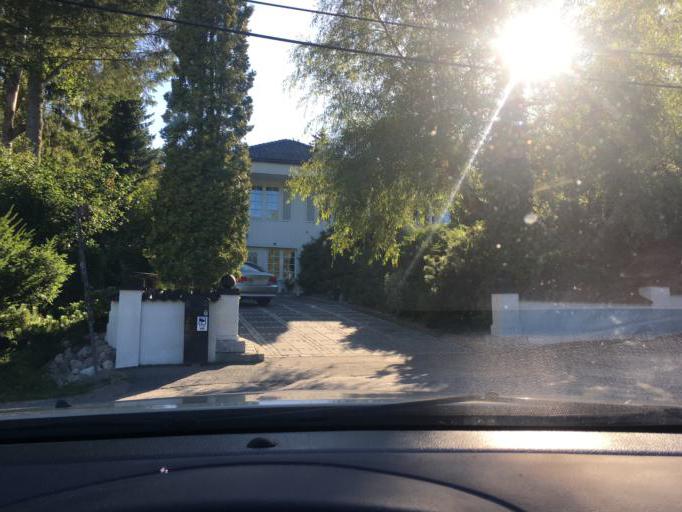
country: SE
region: Stockholm
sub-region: Nacka Kommun
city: Boo
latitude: 59.3236
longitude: 18.2447
